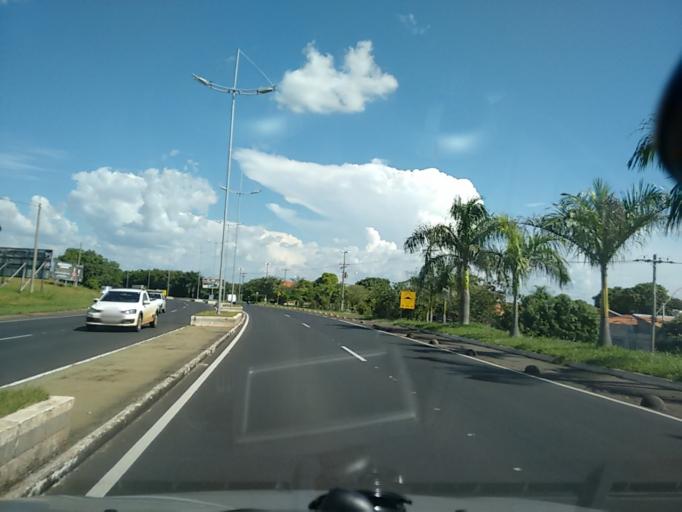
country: BR
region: Sao Paulo
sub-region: Pompeia
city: Pompeia
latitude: -22.1158
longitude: -50.1575
